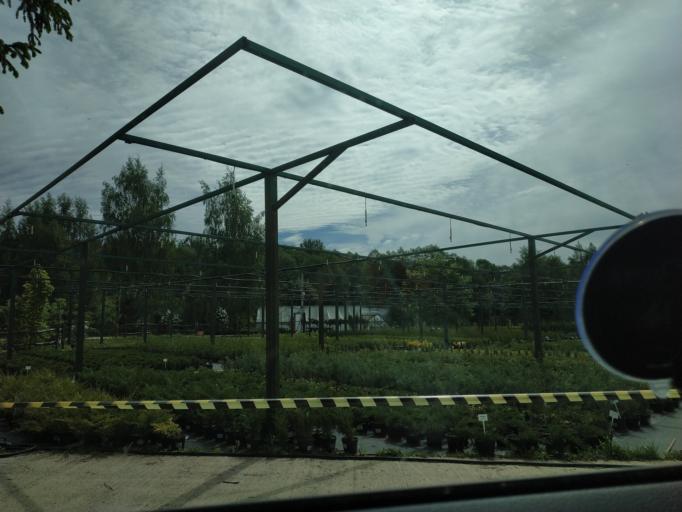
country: RU
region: Moskovskaya
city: Ramenskoye
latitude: 55.5487
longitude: 38.2988
